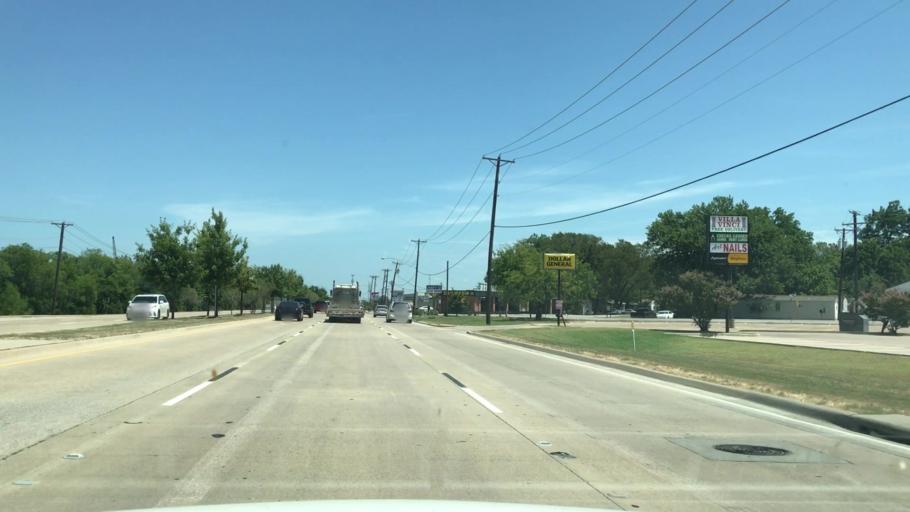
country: US
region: Texas
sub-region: Collin County
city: Wylie
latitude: 33.0147
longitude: -96.5354
